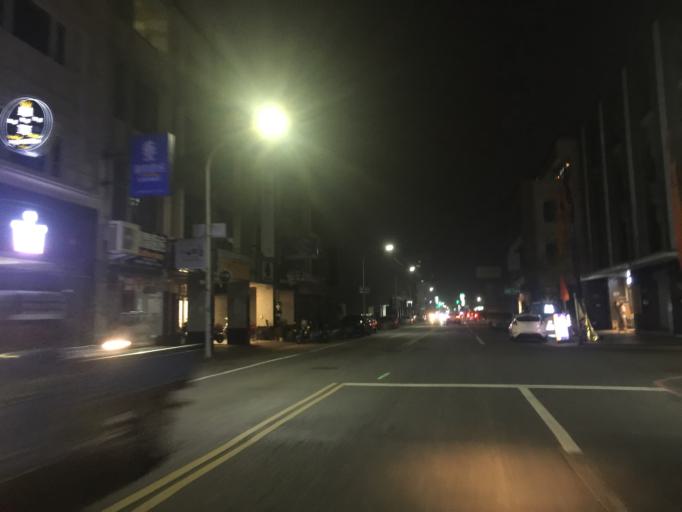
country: TW
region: Taiwan
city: Xinying
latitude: 23.3135
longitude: 120.3232
